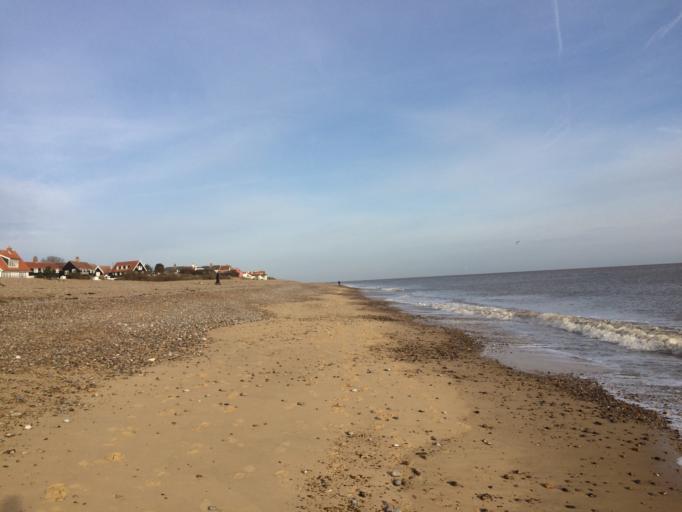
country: GB
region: England
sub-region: Suffolk
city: Aldeburgh
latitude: 52.1774
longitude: 1.6158
